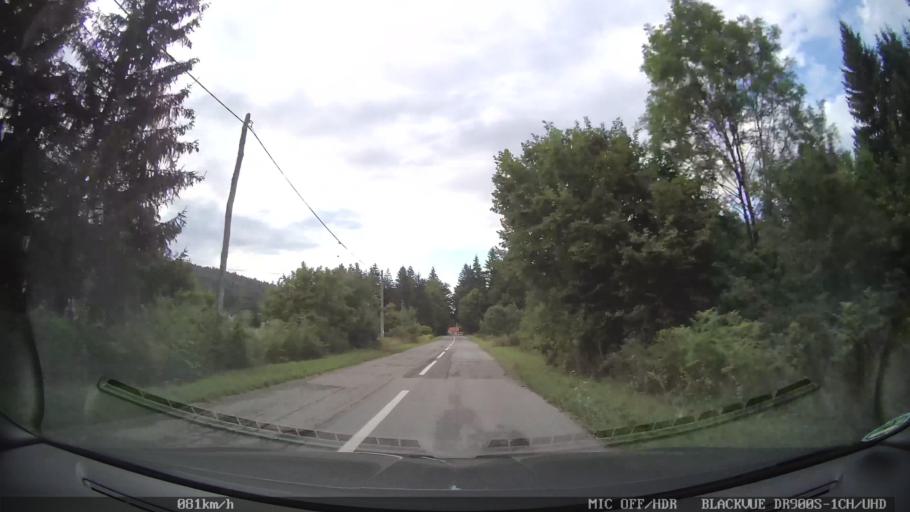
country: HR
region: Licko-Senjska
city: Jezerce
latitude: 44.9534
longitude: 15.5292
